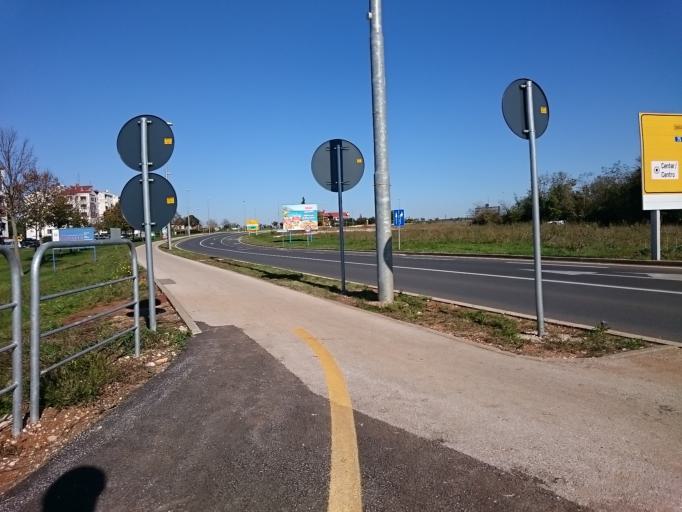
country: HR
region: Istarska
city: Umag
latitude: 45.4282
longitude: 13.5300
